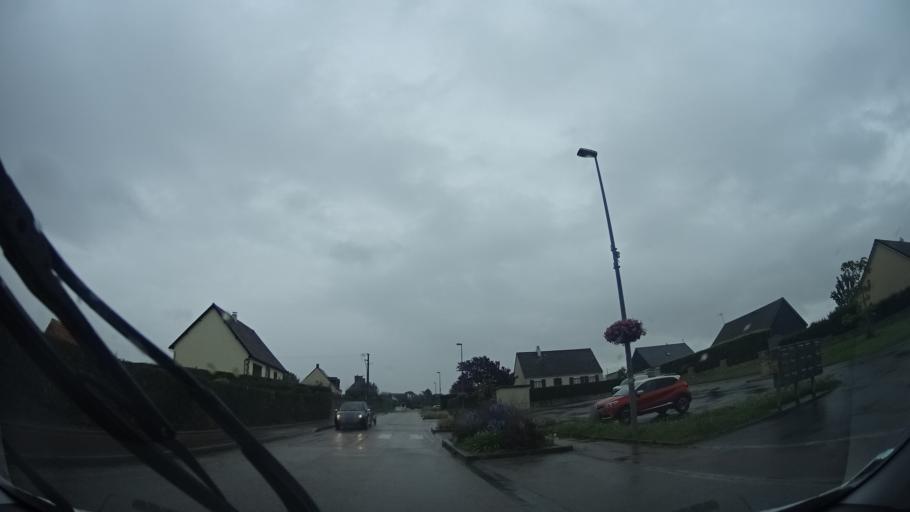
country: FR
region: Lower Normandy
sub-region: Departement de la Manche
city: Urville-Nacqueville
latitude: 49.5973
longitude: -1.7777
